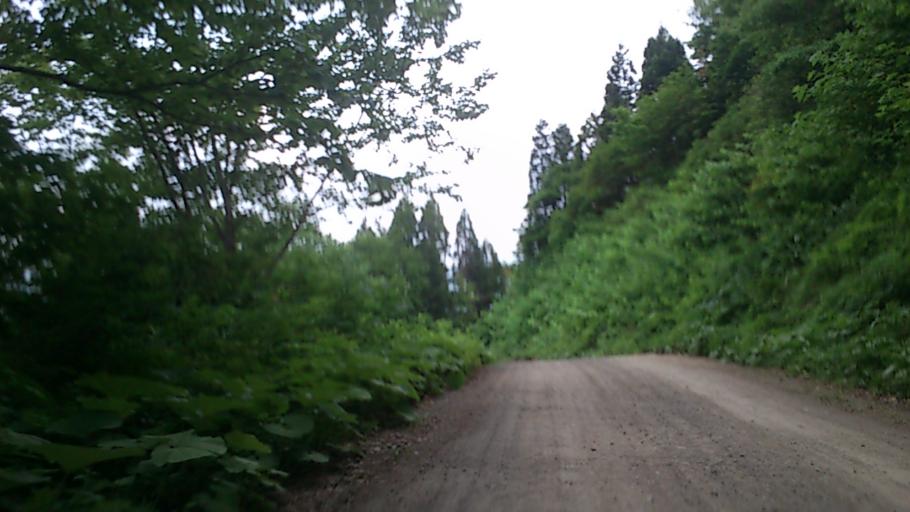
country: JP
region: Aomori
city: Hirosaki
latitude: 40.5529
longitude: 140.1789
